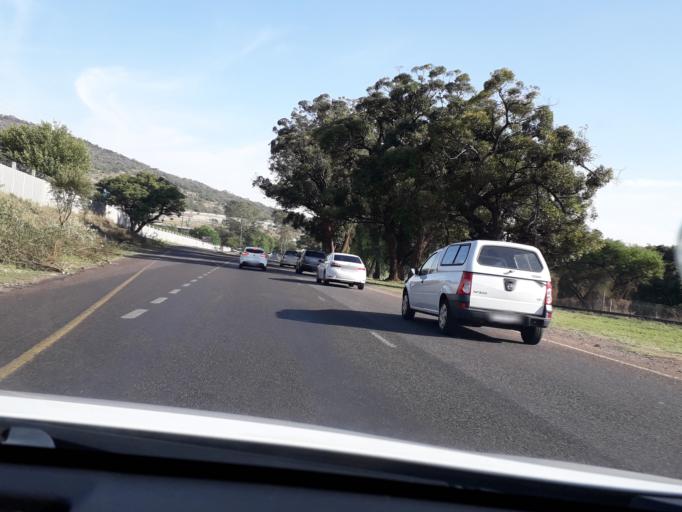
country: ZA
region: Gauteng
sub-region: City of Tshwane Metropolitan Municipality
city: Pretoria
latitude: -25.7849
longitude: 28.1939
